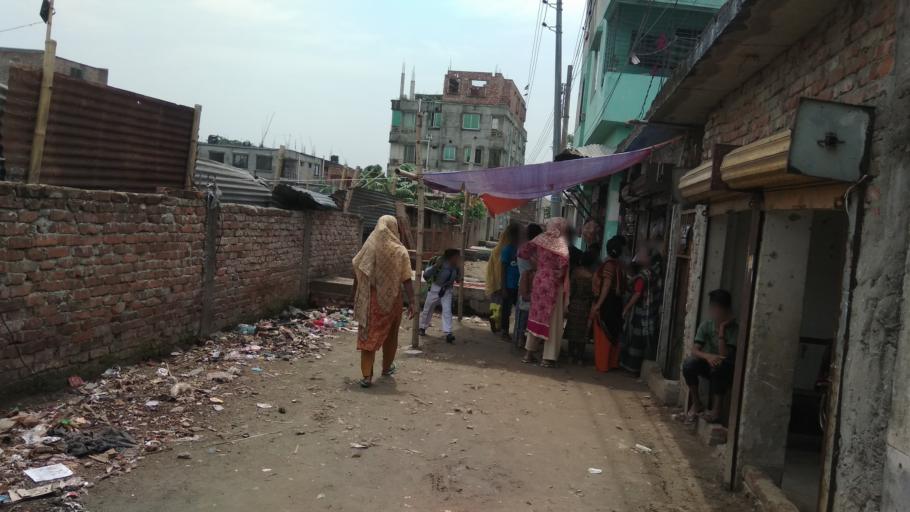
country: BD
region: Dhaka
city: Tungi
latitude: 23.8165
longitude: 90.3791
